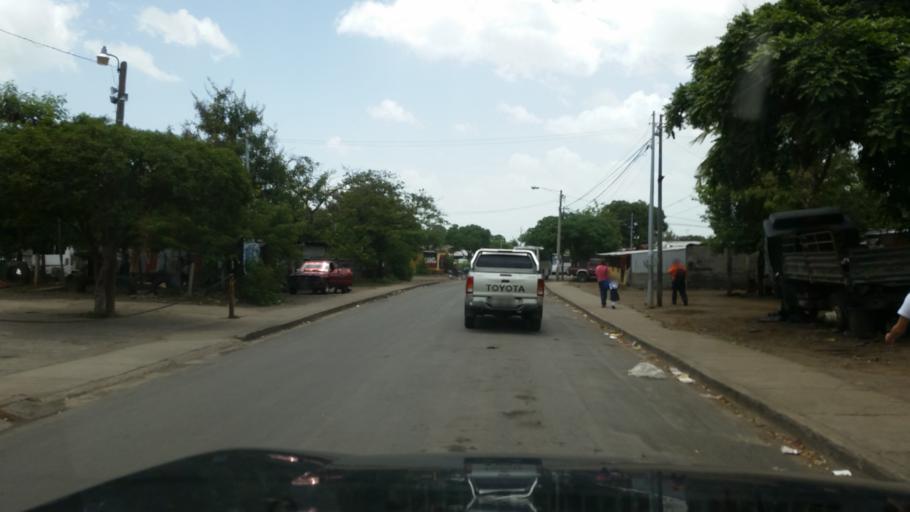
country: NI
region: Managua
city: Managua
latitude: 12.1362
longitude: -86.2091
